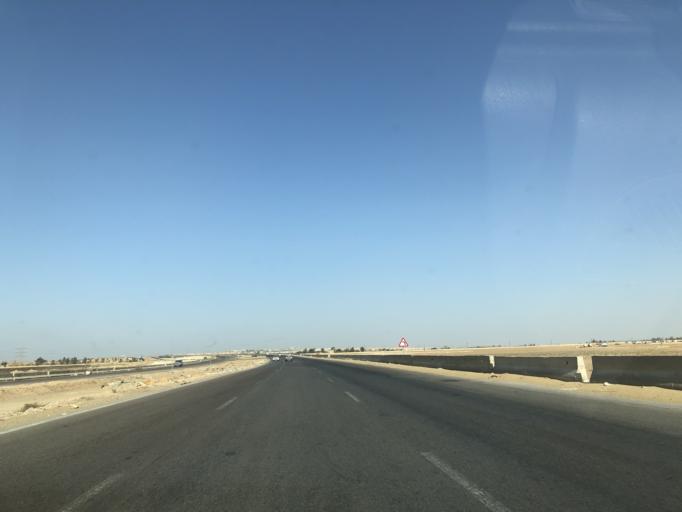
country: EG
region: Muhafazat al Minufiyah
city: Ashmun
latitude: 30.0678
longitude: 30.8971
